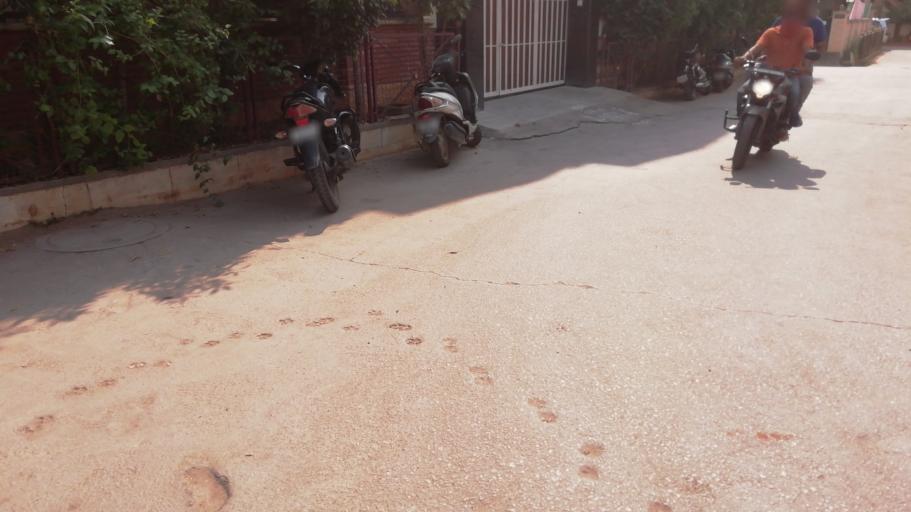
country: IN
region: Telangana
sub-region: Rangareddi
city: Gaddi Annaram
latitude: 17.3639
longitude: 78.5330
